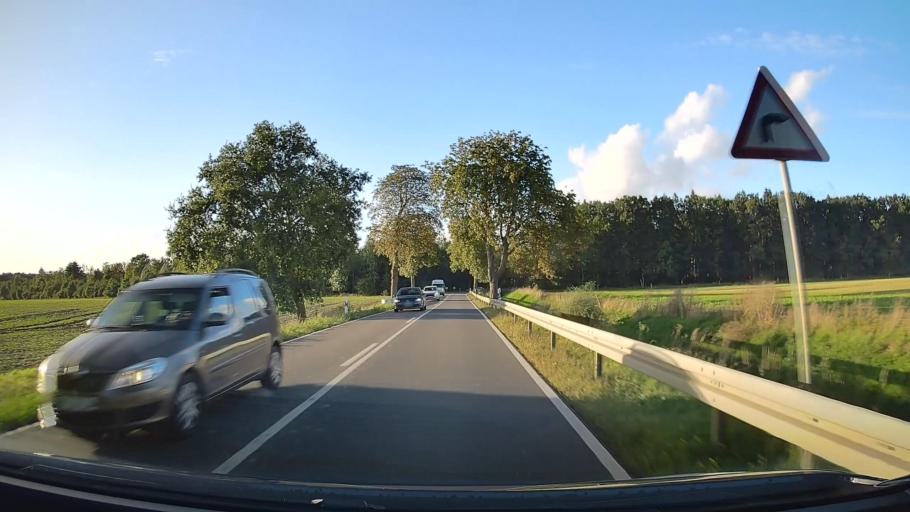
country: DE
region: Mecklenburg-Vorpommern
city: Steinhagen
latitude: 54.1985
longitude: 13.0128
